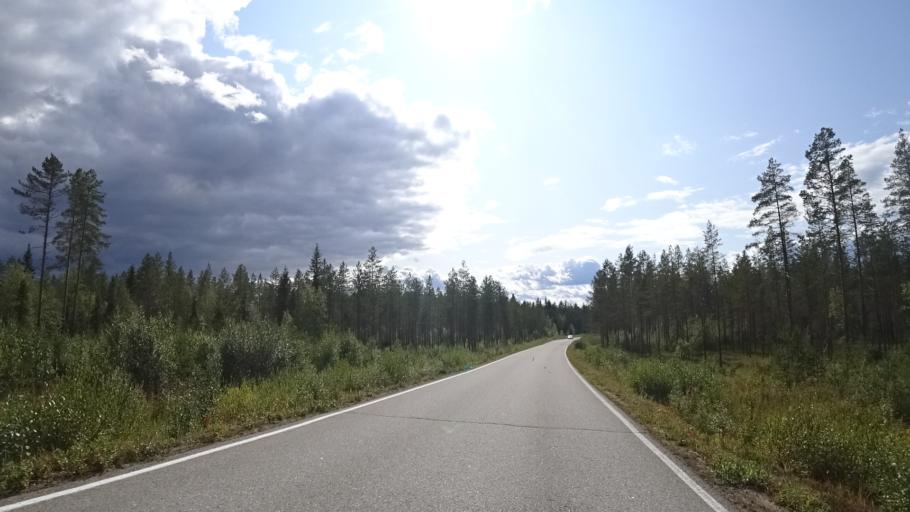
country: FI
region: North Karelia
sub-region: Joensuu
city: Ilomantsi
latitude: 62.4153
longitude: 31.0086
